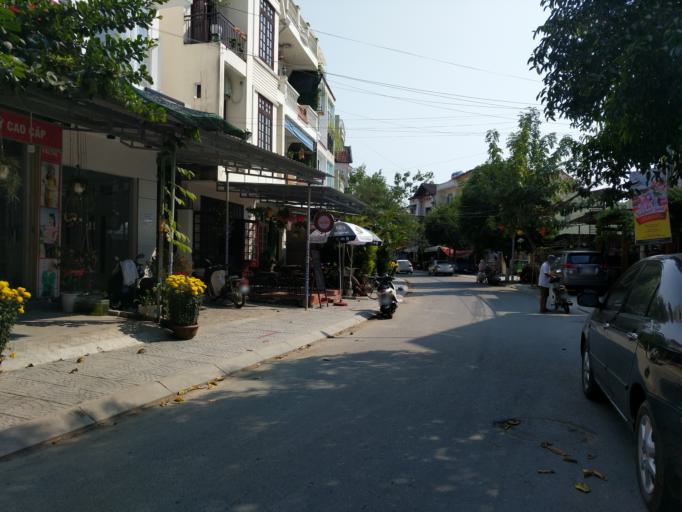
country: VN
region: Quang Nam
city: Hoi An
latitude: 15.8830
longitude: 108.3244
